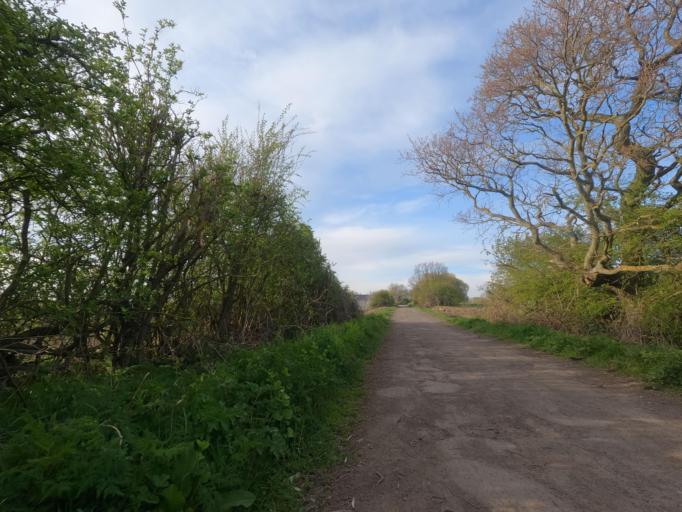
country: GB
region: England
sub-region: Northumberland
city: Cramlington
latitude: 55.0824
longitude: -1.6089
